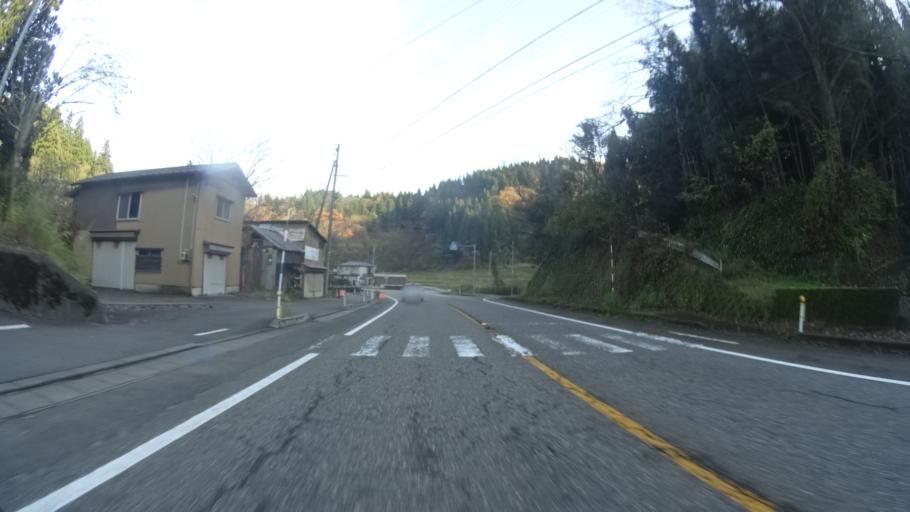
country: JP
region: Niigata
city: Ojiya
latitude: 37.4130
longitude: 138.7073
